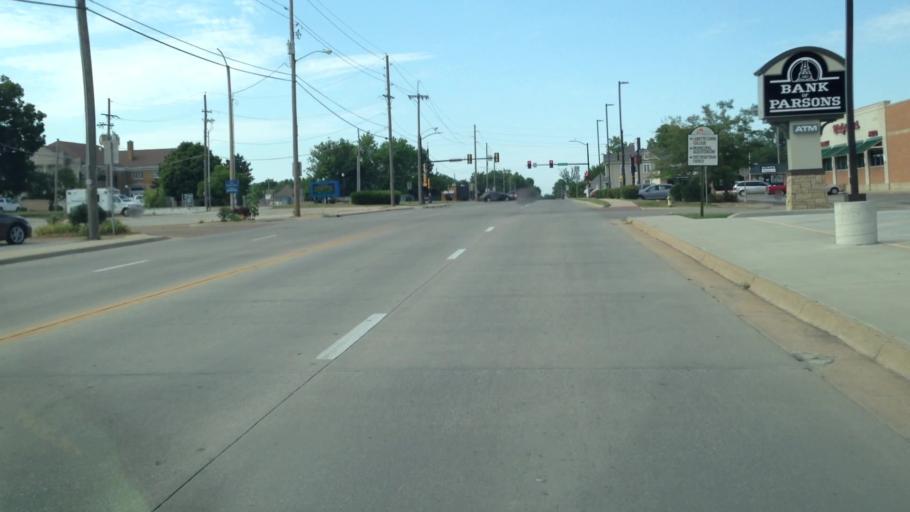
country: US
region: Kansas
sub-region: Labette County
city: Parsons
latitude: 37.3392
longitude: -95.2592
